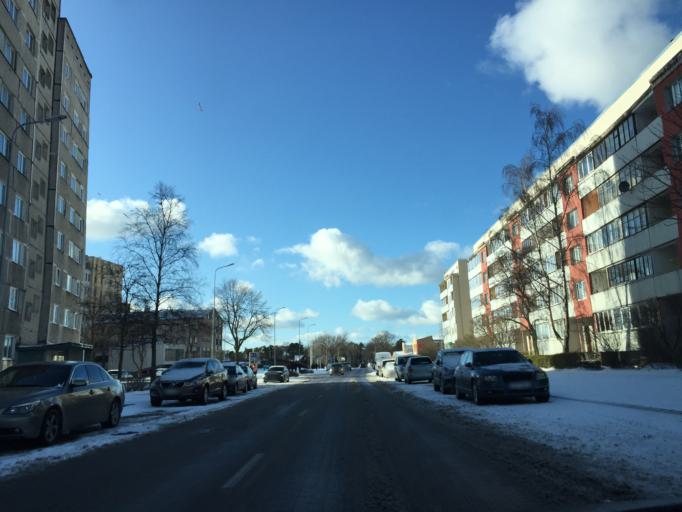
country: LV
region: Ventspils
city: Ventspils
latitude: 57.3846
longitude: 21.5488
